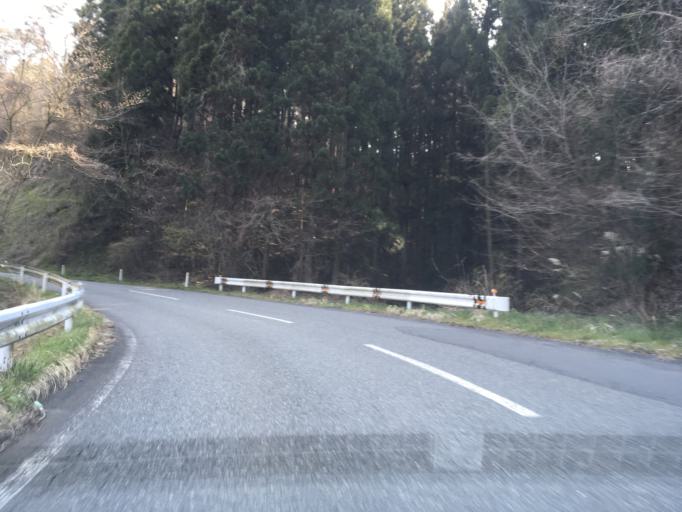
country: JP
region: Iwate
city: Ichinoseki
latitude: 38.8229
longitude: 141.3202
